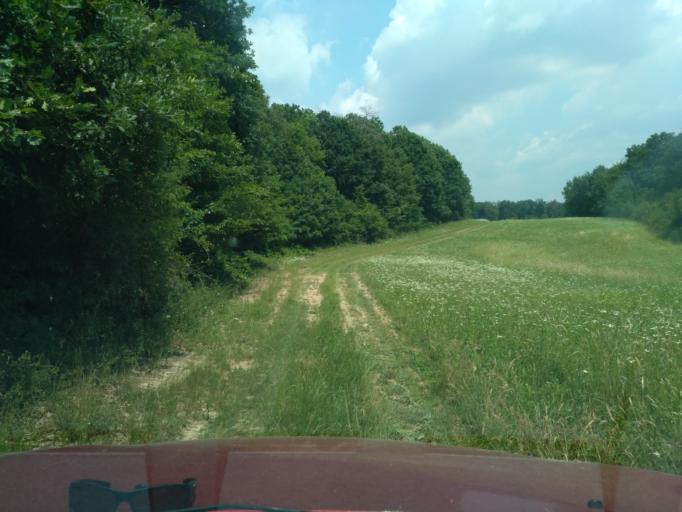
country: SK
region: Kosicky
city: Moldava nad Bodvou
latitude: 48.6289
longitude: 21.0426
